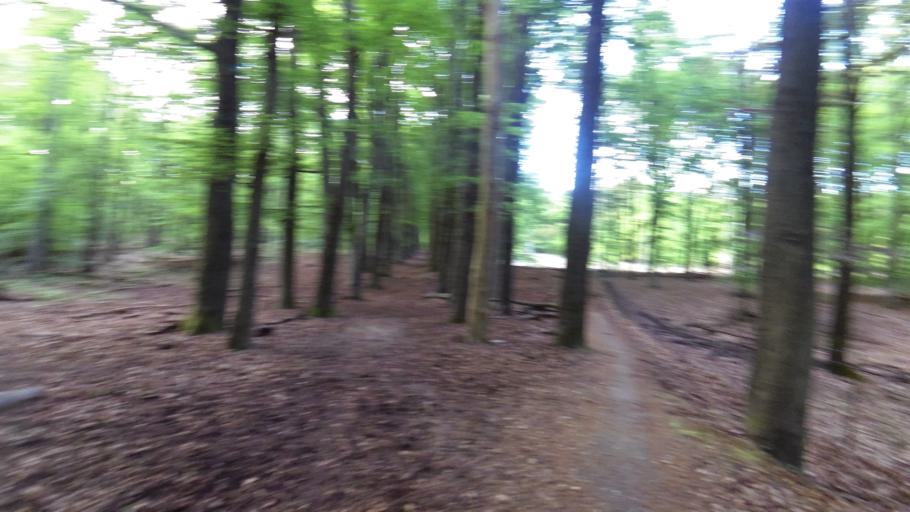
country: NL
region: Gelderland
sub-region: Gemeente Rozendaal
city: Rozendaal
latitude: 52.0137
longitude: 5.9581
